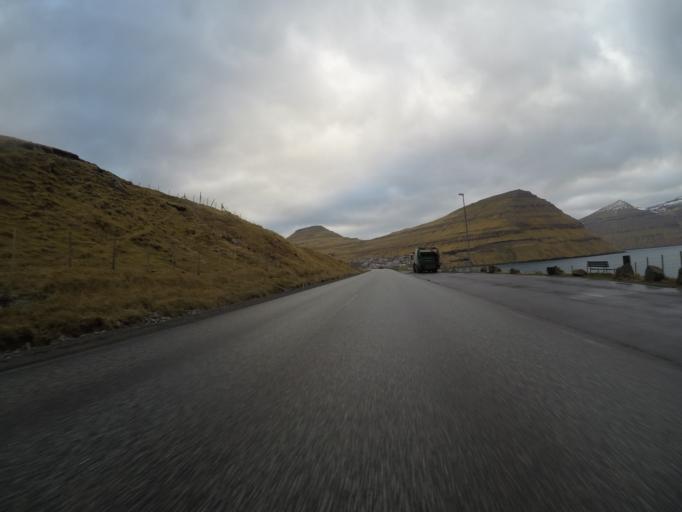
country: FO
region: Nordoyar
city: Klaksvik
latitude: 62.2457
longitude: -6.5870
